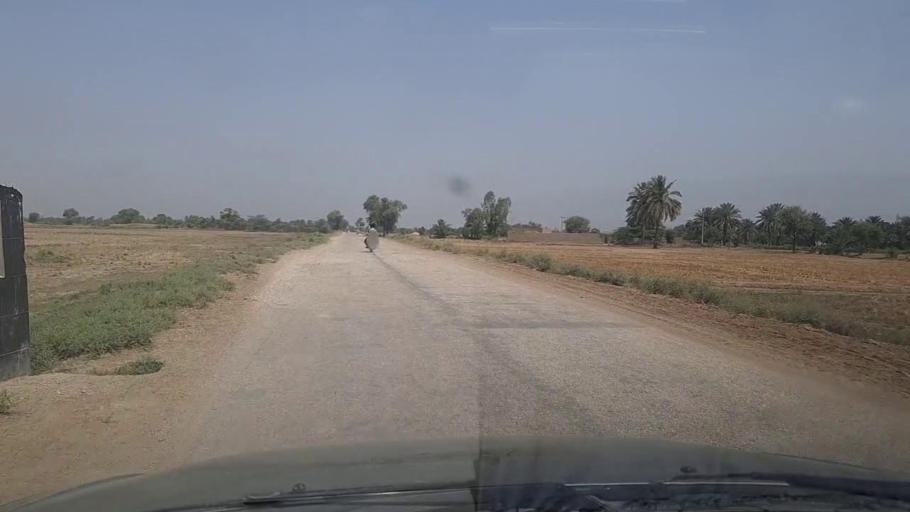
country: PK
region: Sindh
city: Setharja Old
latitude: 27.1378
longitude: 68.5290
